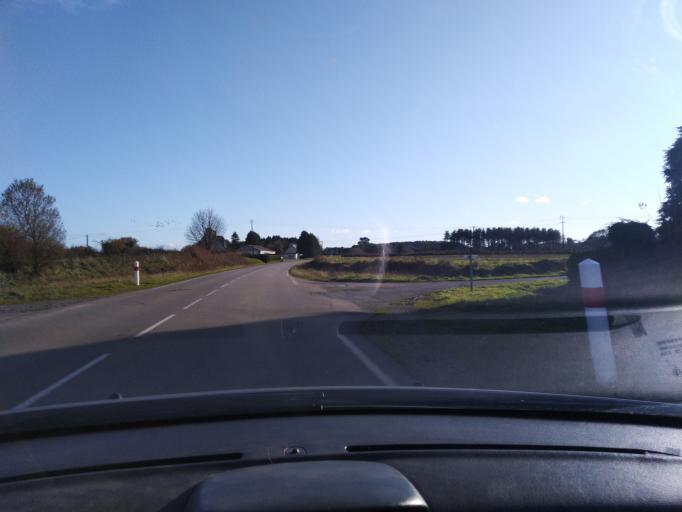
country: FR
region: Brittany
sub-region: Departement du Finistere
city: Guerlesquin
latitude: 48.5382
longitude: -3.5982
